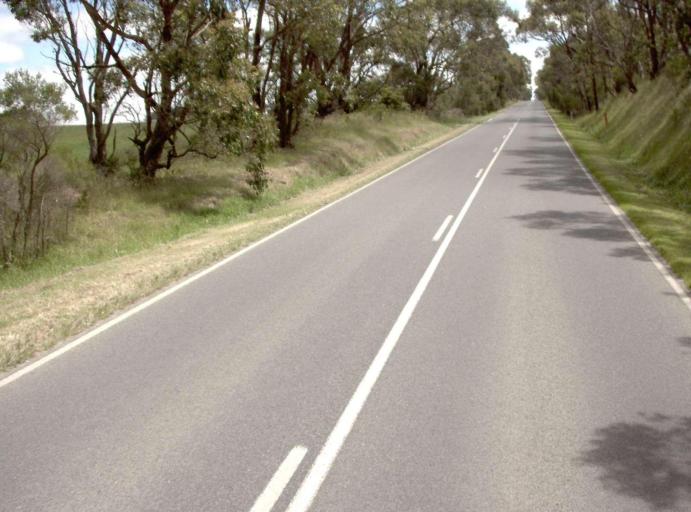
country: AU
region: Victoria
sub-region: Bass Coast
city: North Wonthaggi
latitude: -38.6747
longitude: 146.0308
